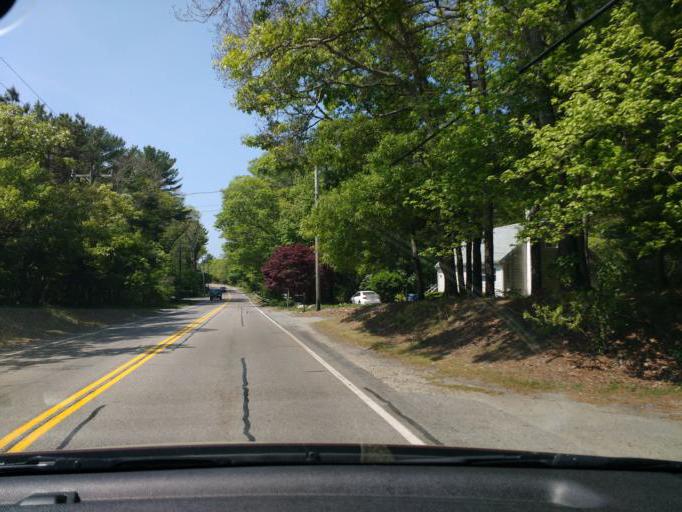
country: US
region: Massachusetts
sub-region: Barnstable County
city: East Falmouth
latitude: 41.5952
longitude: -70.5772
